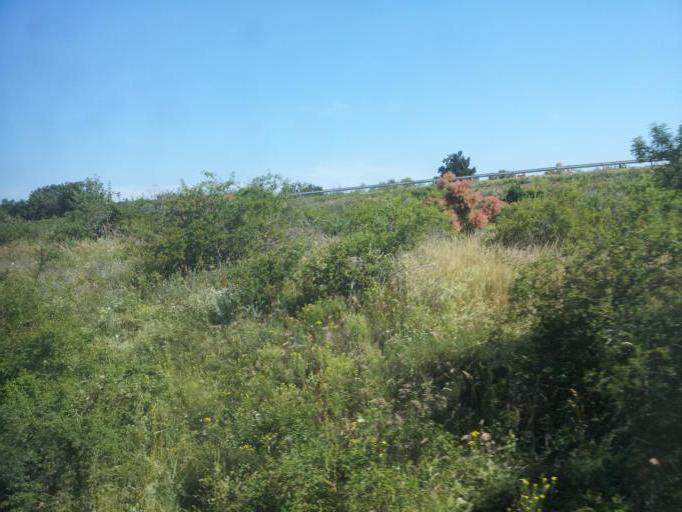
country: HU
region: Veszprem
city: Csopak
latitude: 46.9778
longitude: 17.9519
